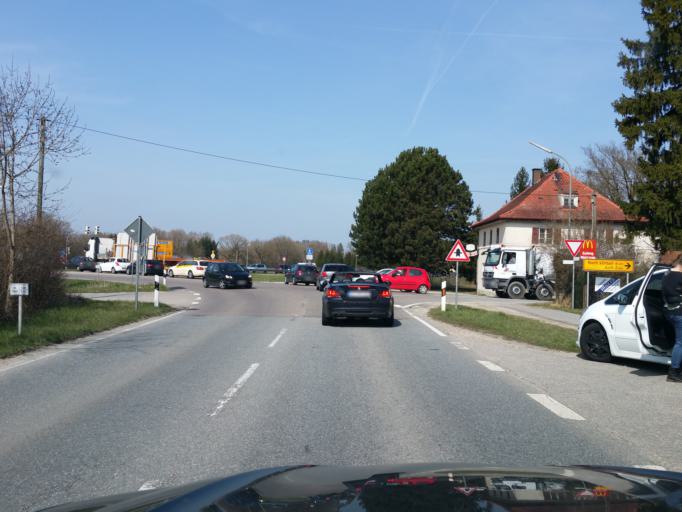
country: DE
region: Bavaria
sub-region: Upper Bavaria
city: Moosburg
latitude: 48.4648
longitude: 11.9538
